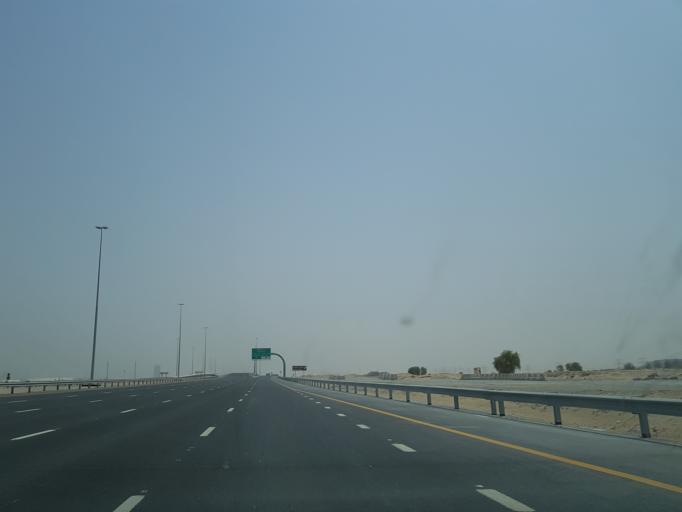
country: AE
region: Dubai
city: Dubai
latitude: 25.0539
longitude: 55.2945
